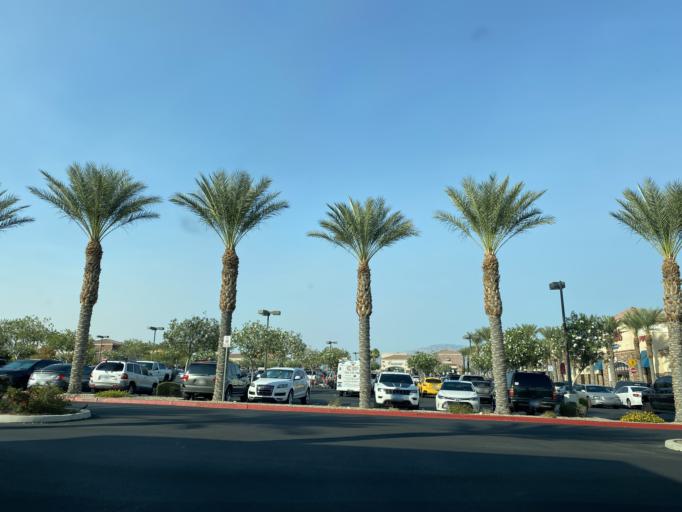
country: US
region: Nevada
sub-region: Clark County
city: Summerlin South
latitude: 36.2898
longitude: -115.2864
